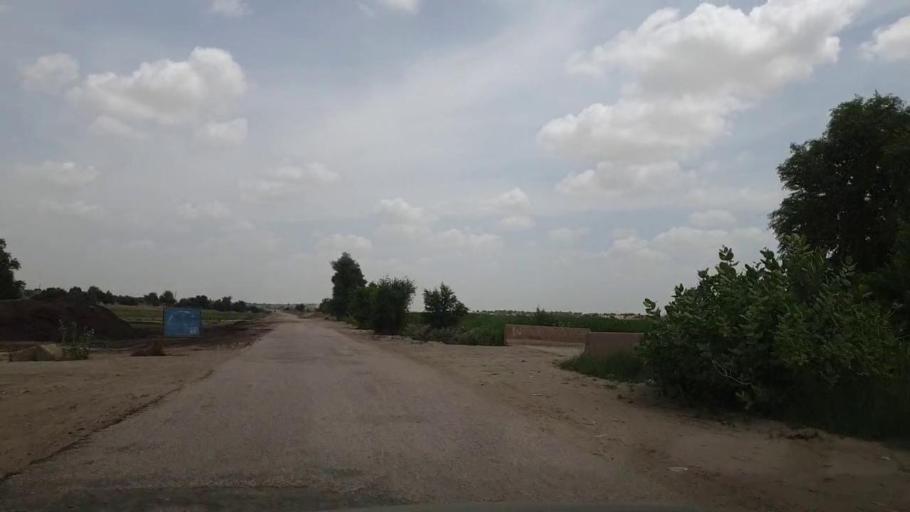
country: PK
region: Sindh
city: Kot Diji
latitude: 27.2044
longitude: 69.1195
